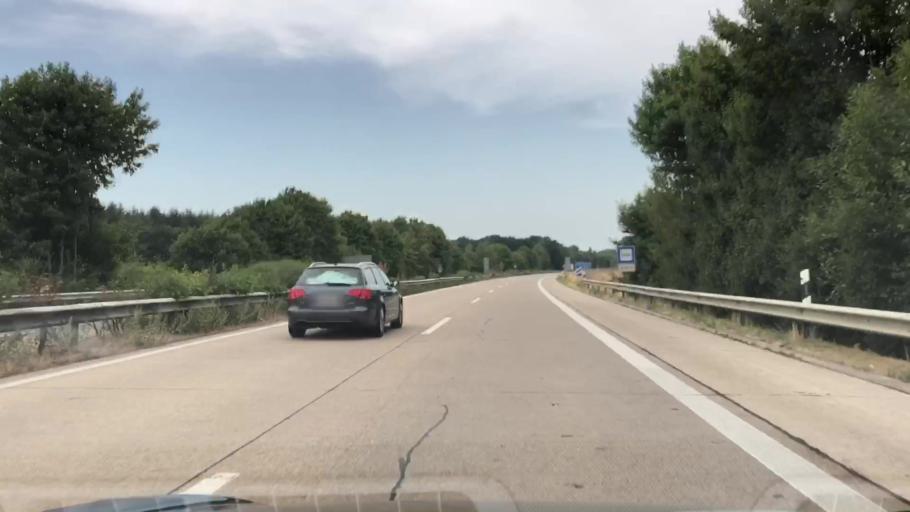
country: DE
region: Lower Saxony
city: Emstek
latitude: 52.8910
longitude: 8.1739
